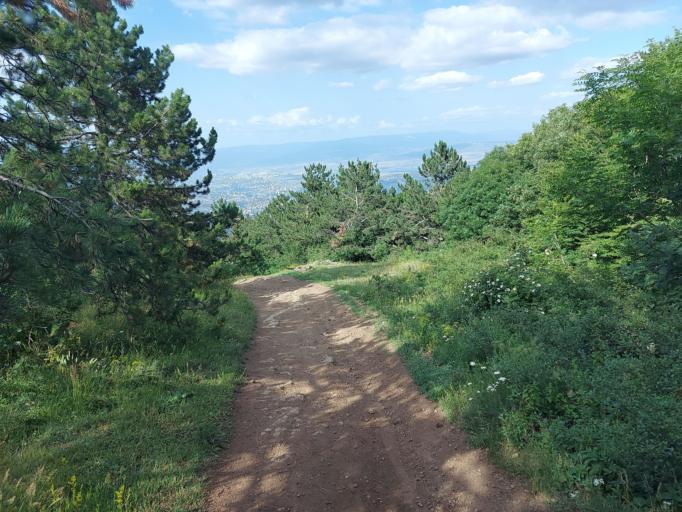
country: GE
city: Tsqnet'i
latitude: 41.6758
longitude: 44.7013
